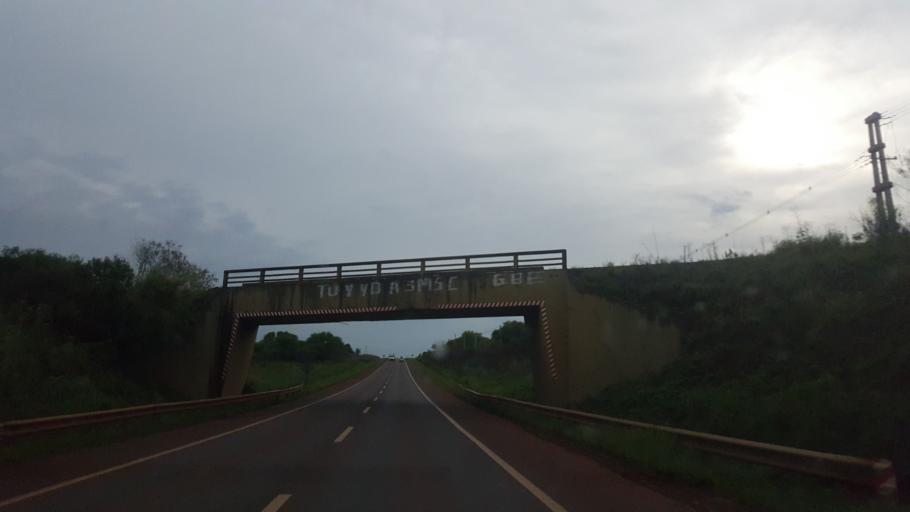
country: AR
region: Misiones
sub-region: Departamento de Apostoles
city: San Jose
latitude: -27.7636
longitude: -55.7966
